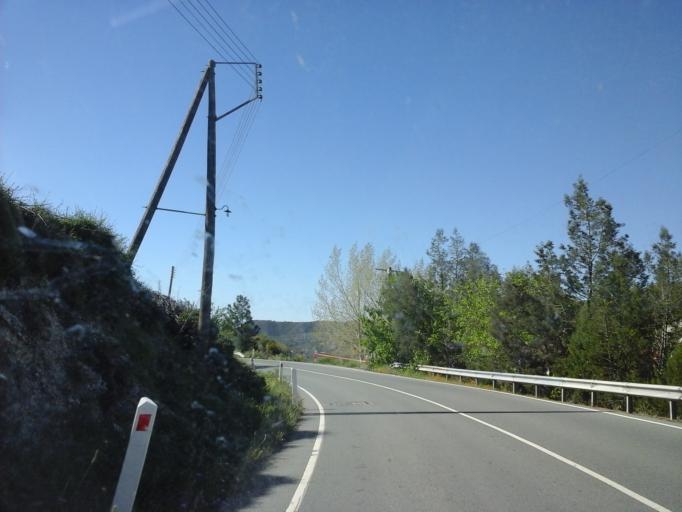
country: CY
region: Limassol
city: Pelendri
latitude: 34.8273
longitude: 32.9097
